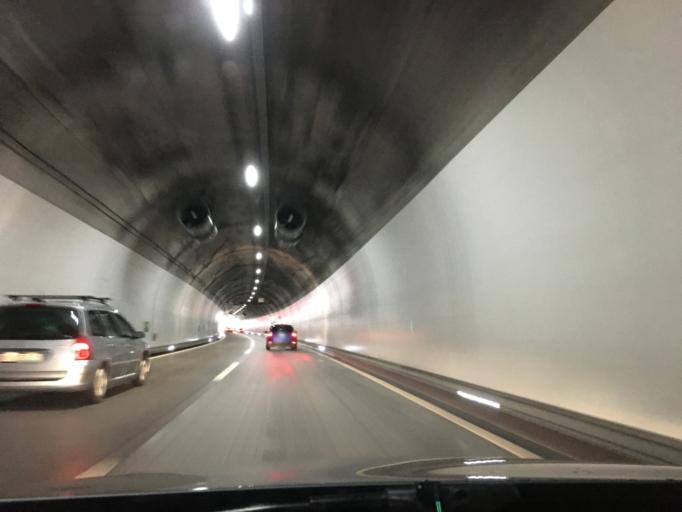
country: CH
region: Saint Gallen
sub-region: Wahlkreis Sarganserland
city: Walenstadt
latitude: 47.1128
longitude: 9.3028
